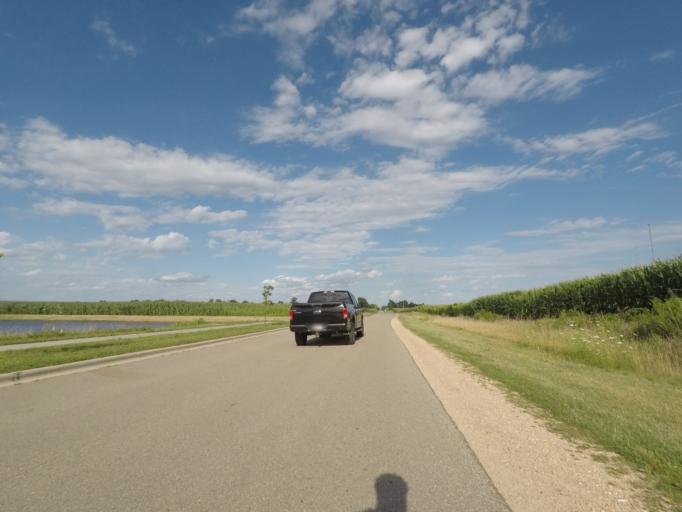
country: US
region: Wisconsin
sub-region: Dane County
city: Middleton
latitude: 43.0675
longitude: -89.5574
